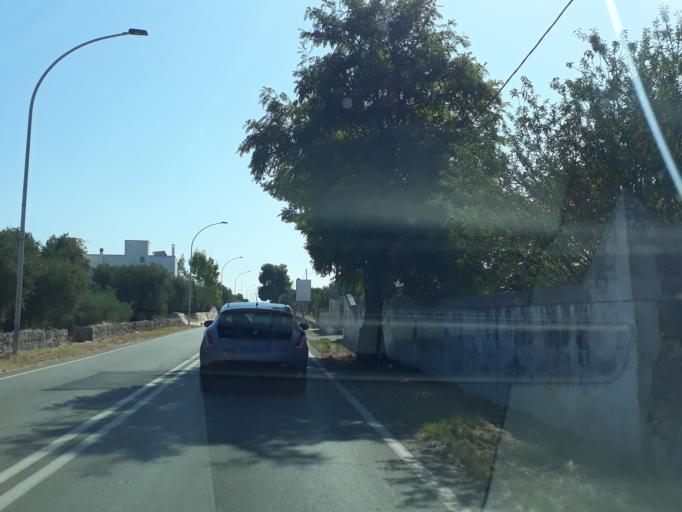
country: IT
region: Apulia
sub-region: Provincia di Bari
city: Monopoli
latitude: 40.9328
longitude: 17.3108
